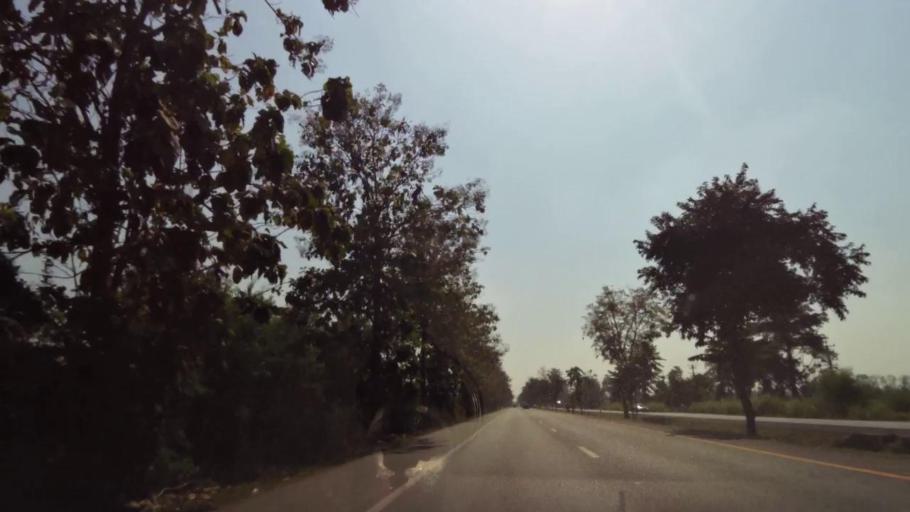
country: TH
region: Phichit
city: Bueng Na Rang
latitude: 16.0865
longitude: 100.1249
